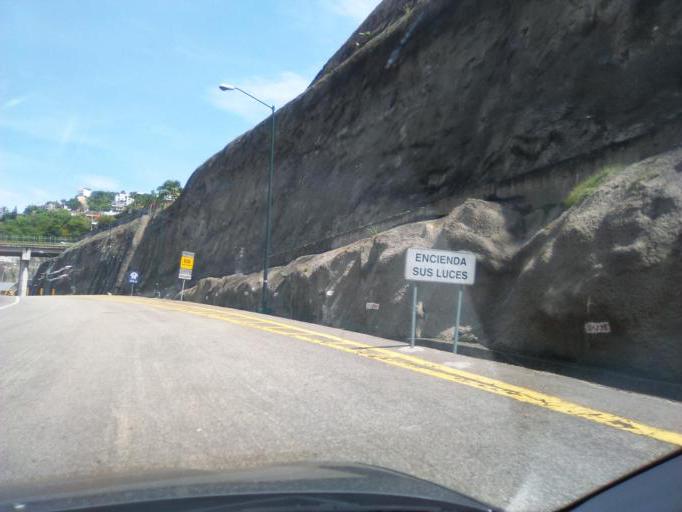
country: MX
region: Guerrero
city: Acapulco de Juarez
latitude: 16.8719
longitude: -99.8679
